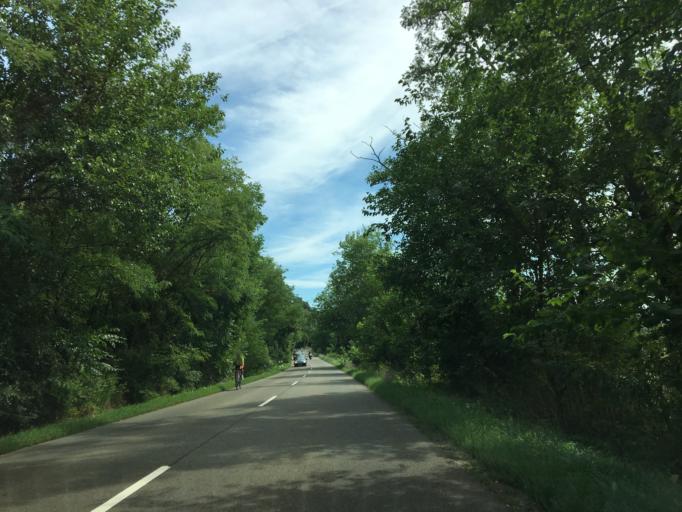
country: HU
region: Pest
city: Szob
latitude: 47.8332
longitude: 18.8452
